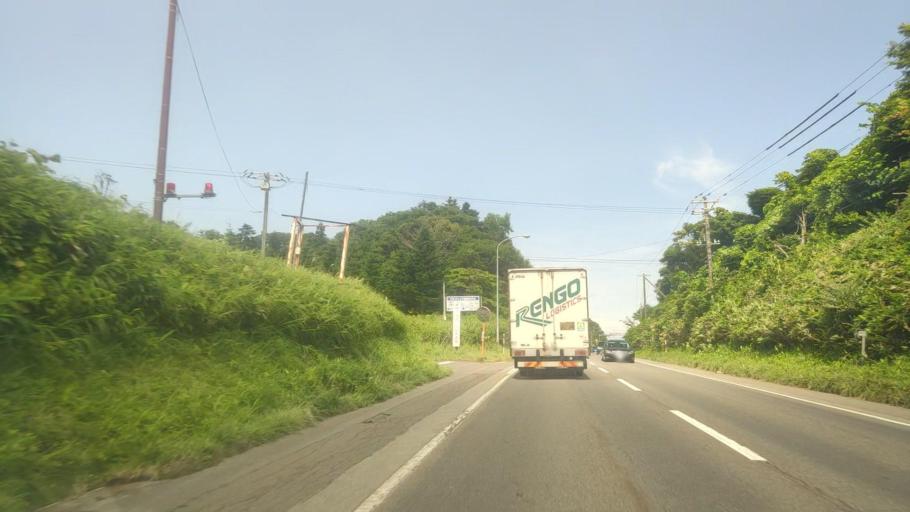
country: JP
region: Hokkaido
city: Nanae
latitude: 42.1677
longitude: 140.4609
